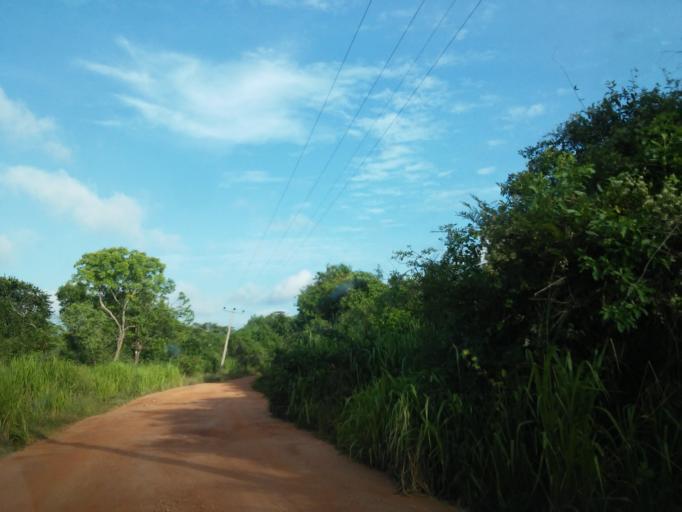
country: LK
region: Central
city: Sigiriya
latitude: 8.1698
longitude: 80.6839
